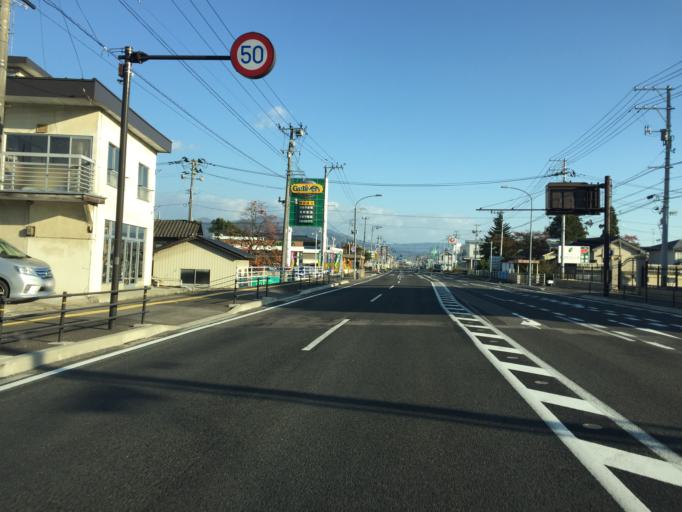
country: JP
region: Fukushima
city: Fukushima-shi
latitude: 37.7913
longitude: 140.4880
